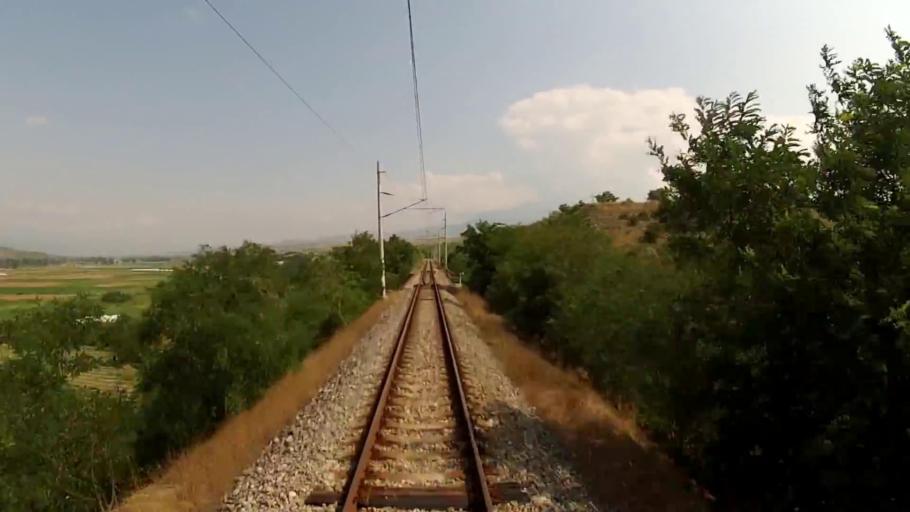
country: BG
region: Blagoevgrad
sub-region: Obshtina Sandanski
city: Sandanski
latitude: 41.5717
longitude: 23.2419
